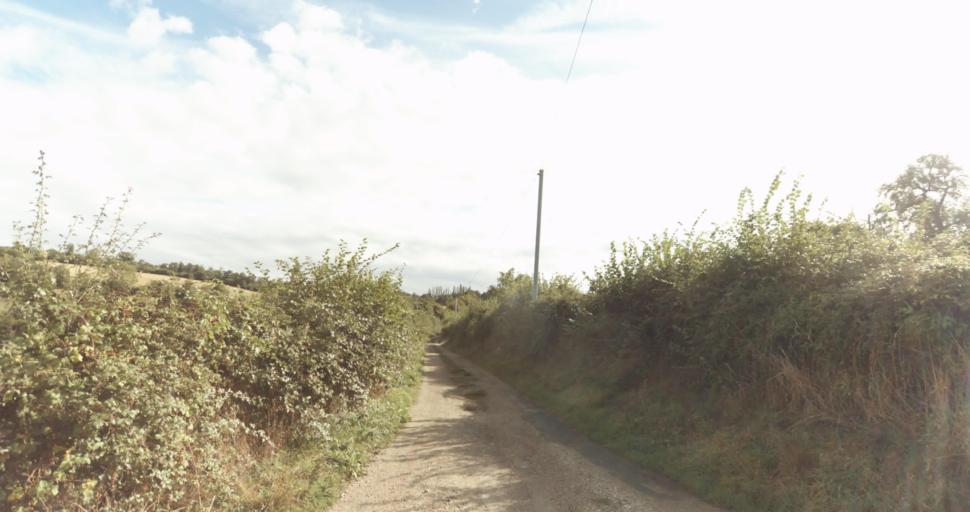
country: FR
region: Lower Normandy
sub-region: Departement de l'Orne
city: Vimoutiers
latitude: 48.8746
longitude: 0.1750
